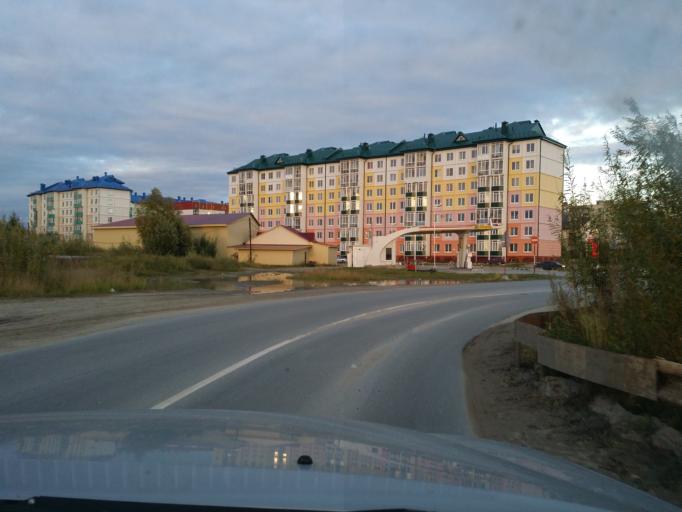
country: RU
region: Khanty-Mansiyskiy Avtonomnyy Okrug
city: Megion
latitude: 61.0346
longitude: 76.0866
